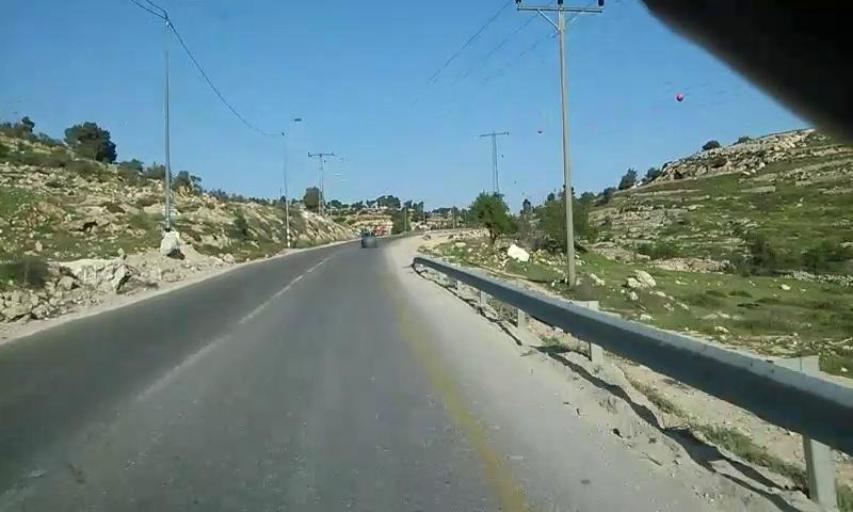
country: PS
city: Khallat ad Dar
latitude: 31.5047
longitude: 35.1278
